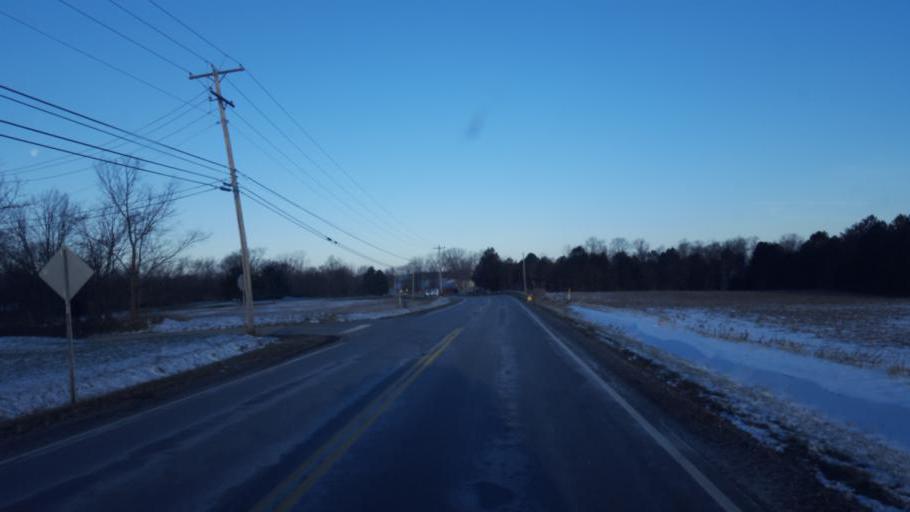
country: US
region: Ohio
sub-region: Morrow County
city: Cardington
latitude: 40.5170
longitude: -82.8662
